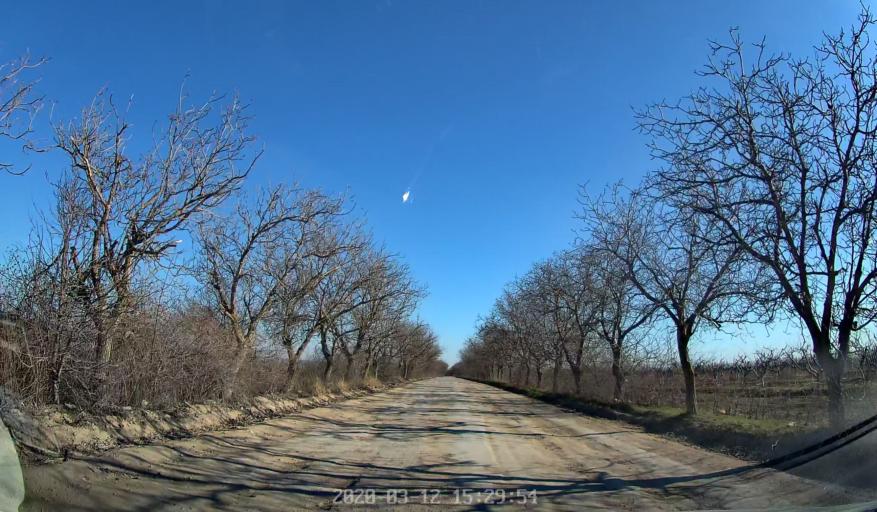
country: MD
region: Chisinau
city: Ciorescu
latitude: 47.1627
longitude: 28.9370
